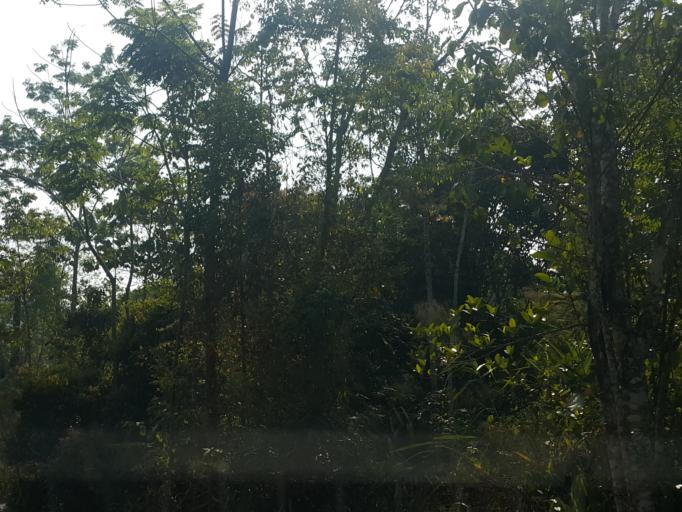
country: TH
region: Chiang Mai
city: Samoeng
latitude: 19.0166
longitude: 98.7605
